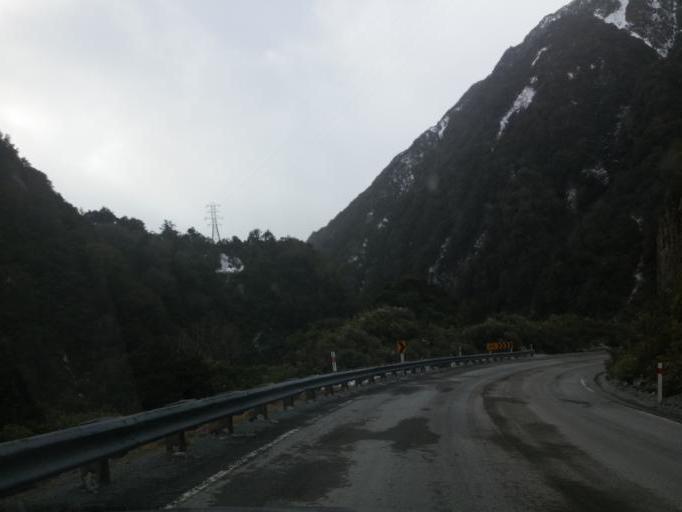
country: NZ
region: West Coast
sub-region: Grey District
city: Greymouth
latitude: -42.8817
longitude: 171.5547
